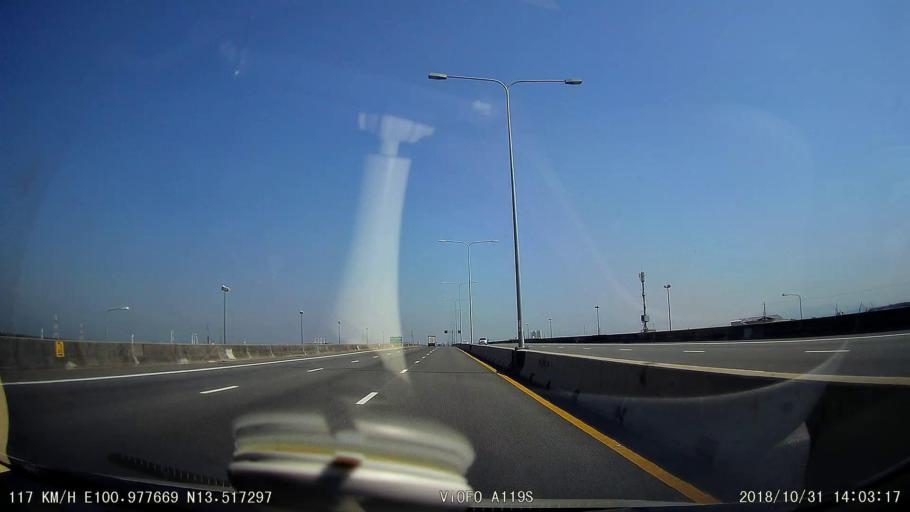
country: TH
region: Chachoengsao
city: Bang Pakong
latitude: 13.5171
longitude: 100.9780
